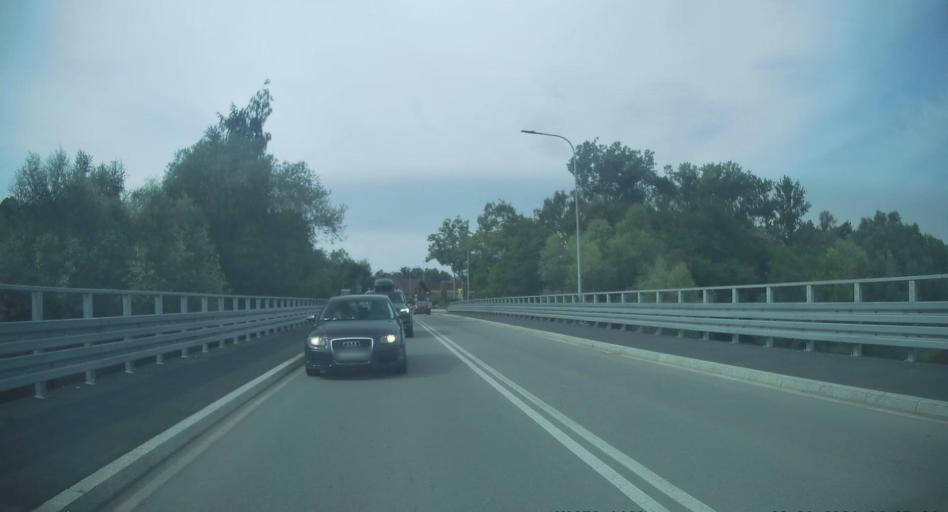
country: PL
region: Lesser Poland Voivodeship
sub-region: Powiat myslenicki
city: Myslenice
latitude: 49.8240
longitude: 19.9448
